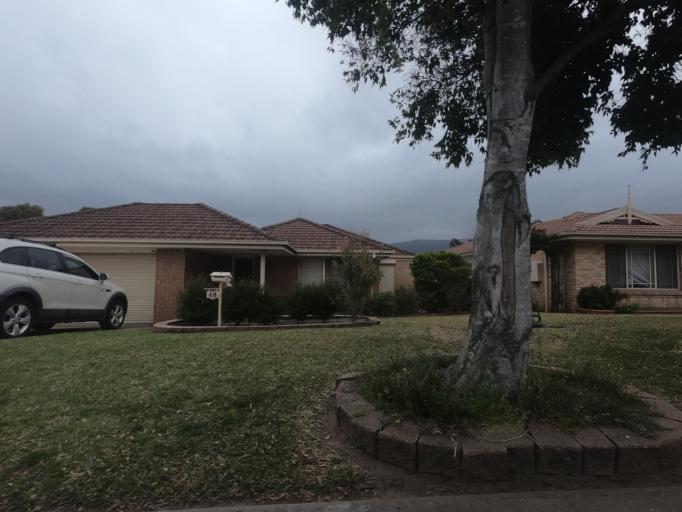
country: AU
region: New South Wales
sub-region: Wollongong
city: Dapto
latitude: -34.4862
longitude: 150.7749
